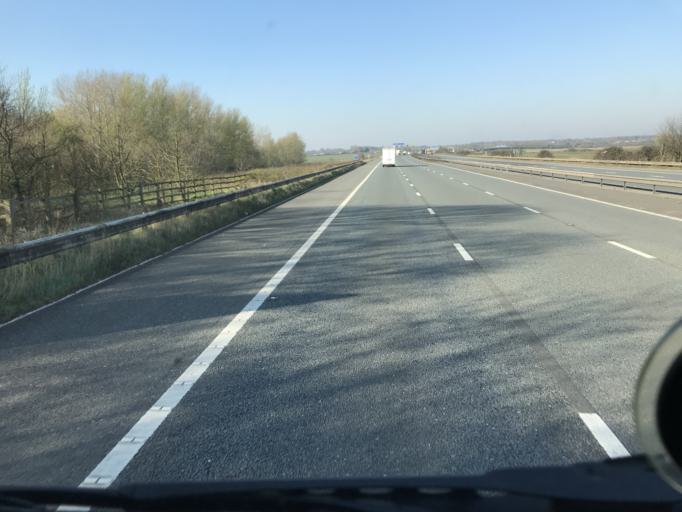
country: GB
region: England
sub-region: Cheshire West and Chester
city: Stoke
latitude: 53.2521
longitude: -2.8402
